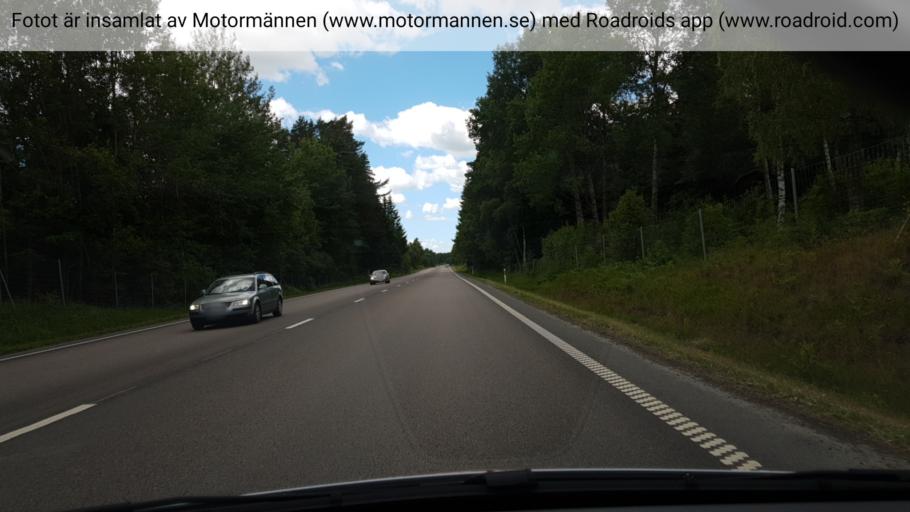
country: SE
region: Vaestra Goetaland
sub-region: Lidkopings Kommun
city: Vinninga
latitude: 58.4293
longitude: 13.3126
